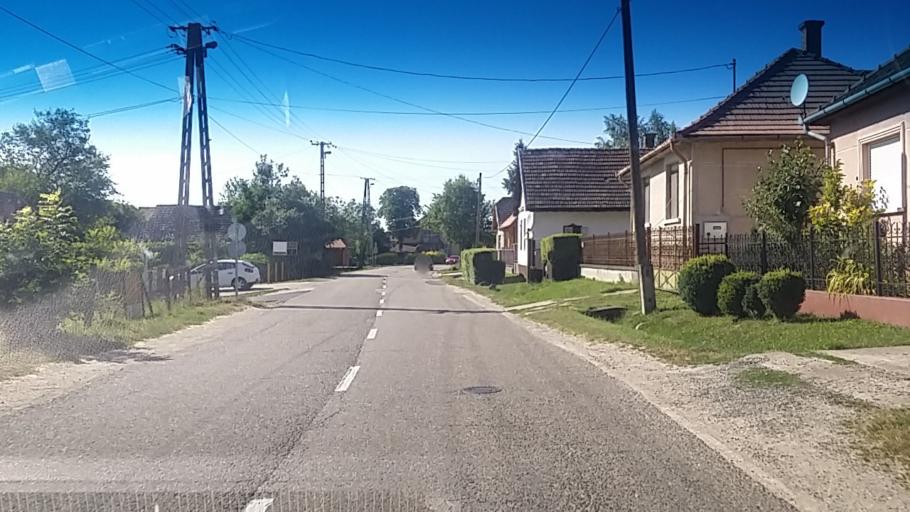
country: HU
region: Nograd
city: Retsag
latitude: 47.9257
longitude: 19.1743
